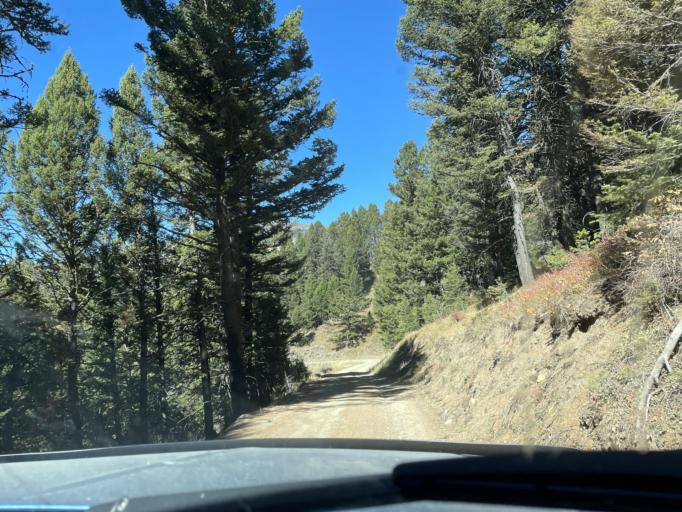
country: US
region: Montana
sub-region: Broadwater County
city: Townsend
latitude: 46.5082
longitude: -111.2833
